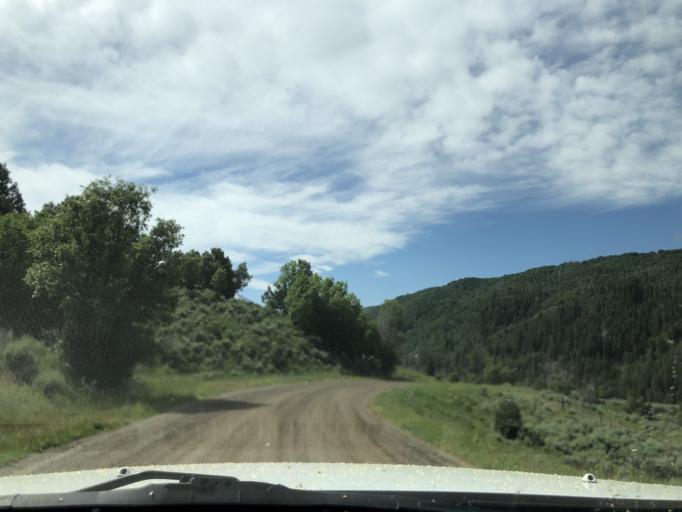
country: US
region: Colorado
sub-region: Delta County
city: Paonia
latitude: 38.9987
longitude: -107.3529
